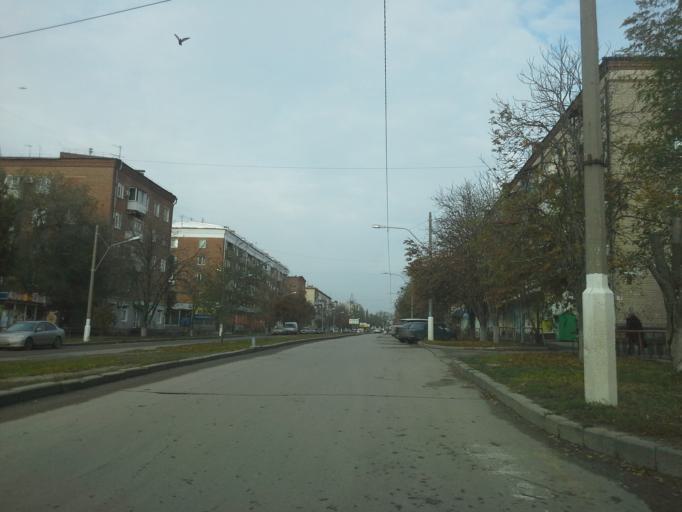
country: RU
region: Volgograd
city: Vodstroy
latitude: 48.7819
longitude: 44.5680
